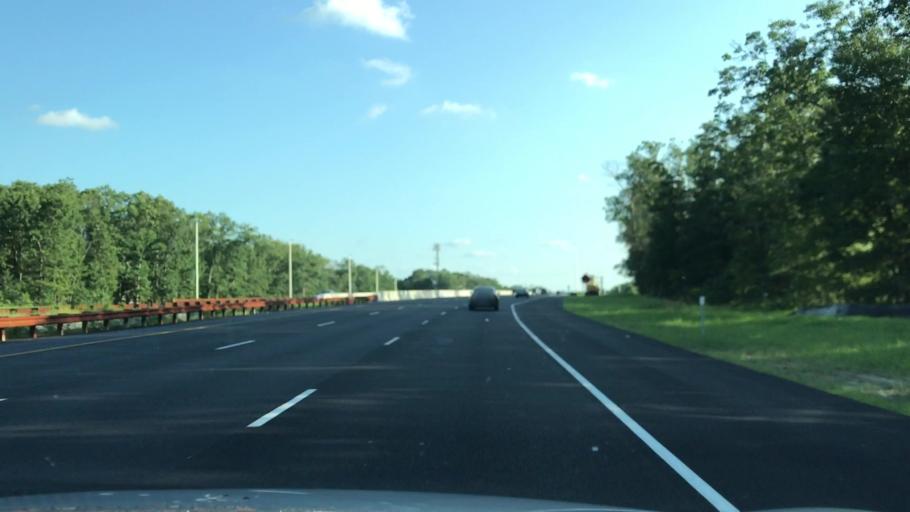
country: US
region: New Jersey
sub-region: Atlantic County
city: Pomona
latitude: 39.4546
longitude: -74.5354
